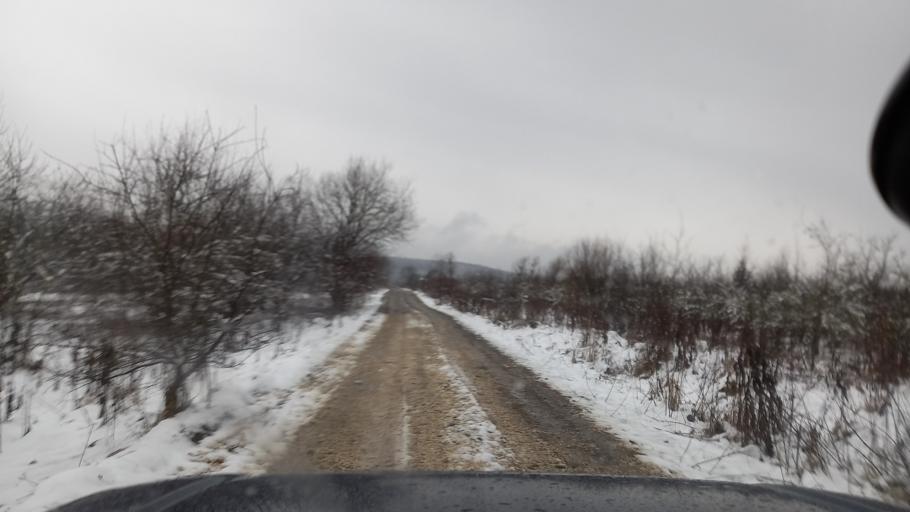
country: RU
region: Adygeya
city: Abadzekhskaya
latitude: 44.3739
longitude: 40.2520
